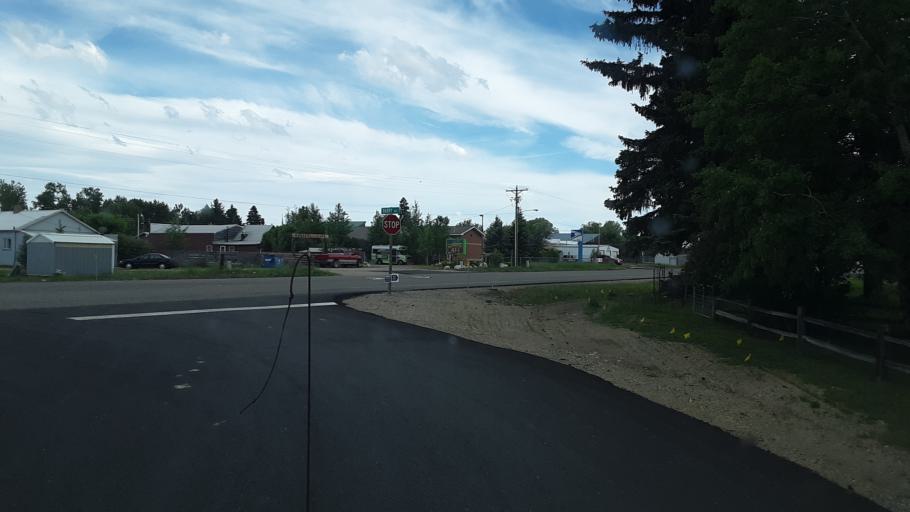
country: US
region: Montana
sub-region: Carbon County
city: Red Lodge
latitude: 45.3600
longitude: -109.1682
